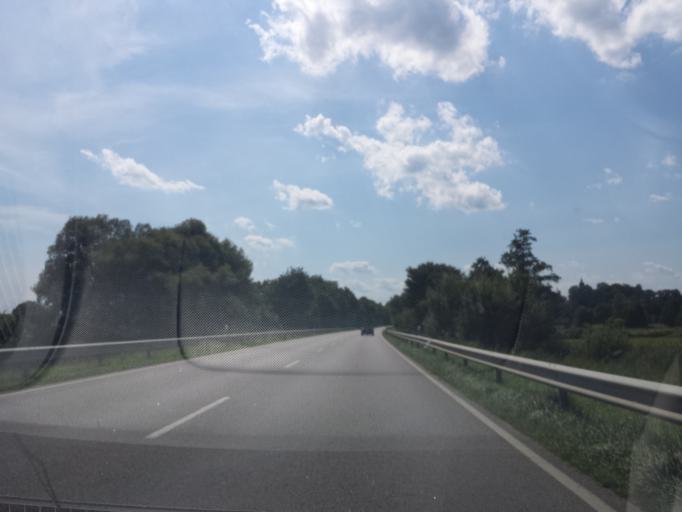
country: DE
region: Bavaria
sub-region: Lower Bavaria
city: Biburg
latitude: 48.8053
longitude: 11.8591
